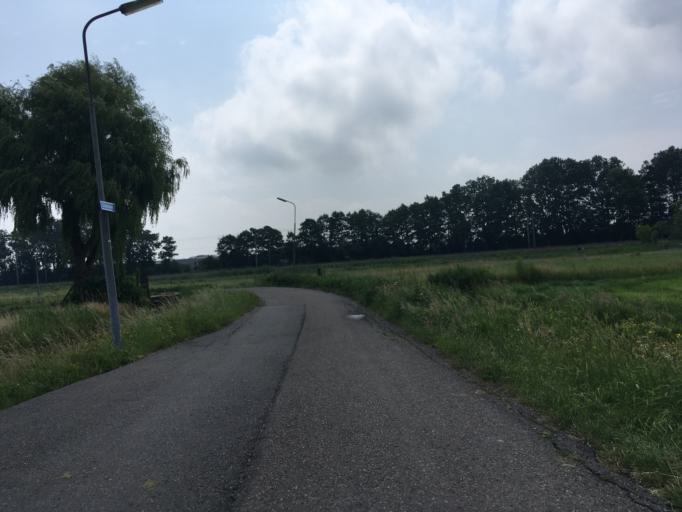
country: NL
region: North Holland
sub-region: Gemeente Haarlem
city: Haarlem
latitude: 52.3872
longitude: 4.7148
